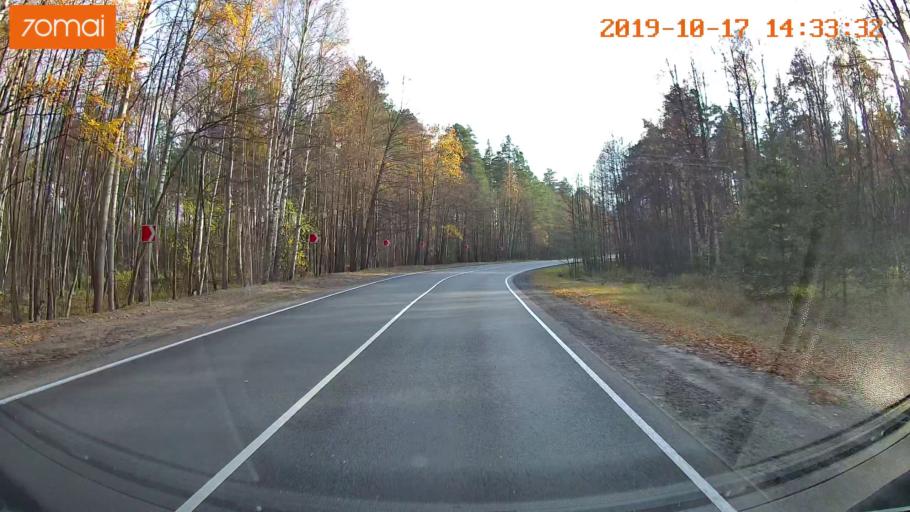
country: RU
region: Rjazan
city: Solotcha
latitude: 54.9227
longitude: 39.9976
